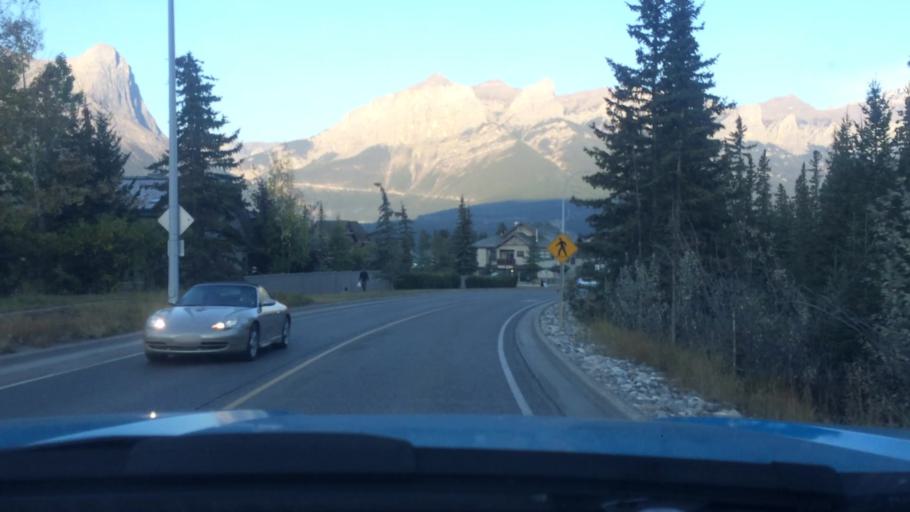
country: CA
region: Alberta
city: Canmore
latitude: 51.0868
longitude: -115.3292
